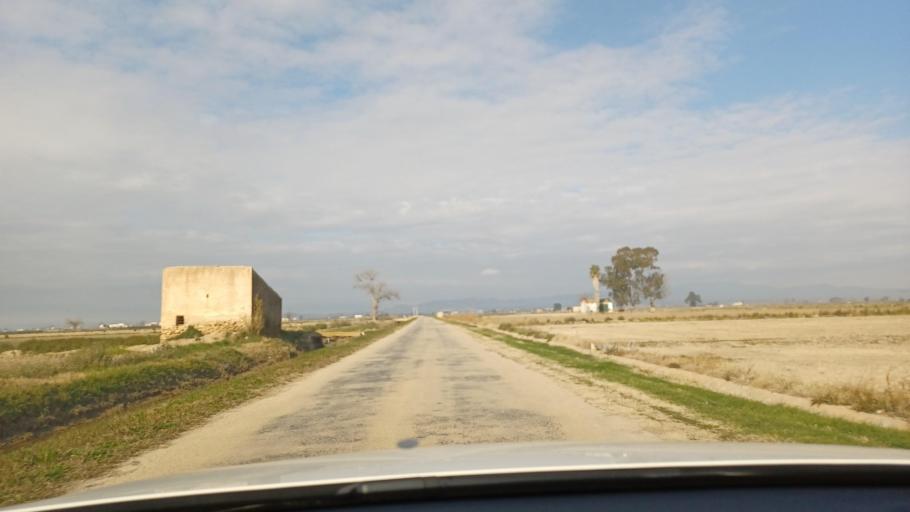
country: ES
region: Catalonia
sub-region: Provincia de Tarragona
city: Deltebre
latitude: 40.6855
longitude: 0.6544
